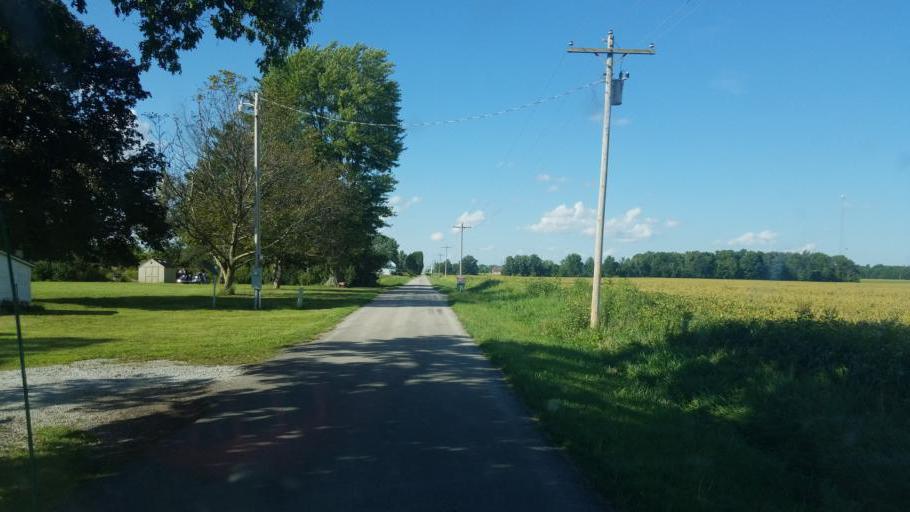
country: US
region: Ohio
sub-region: Marion County
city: Marion
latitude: 40.6236
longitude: -83.2694
